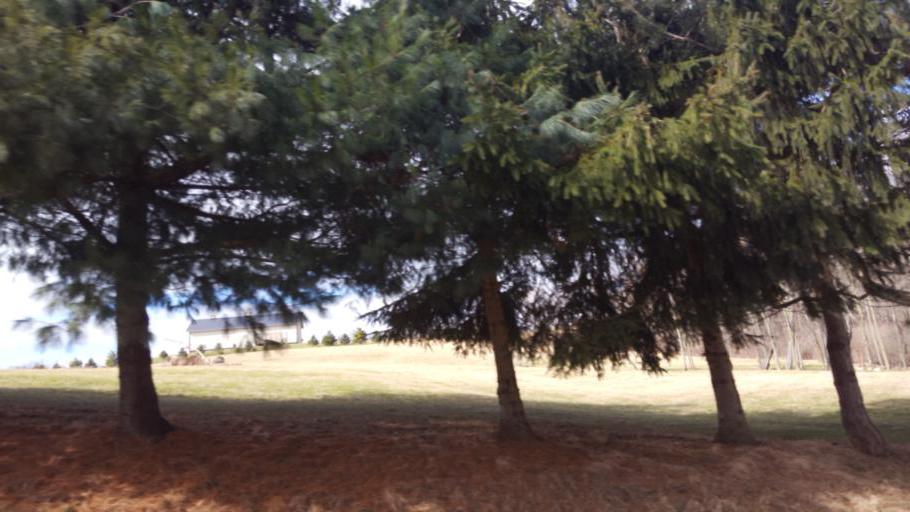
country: US
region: Ohio
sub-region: Sandusky County
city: Bellville
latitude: 40.5749
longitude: -82.5096
